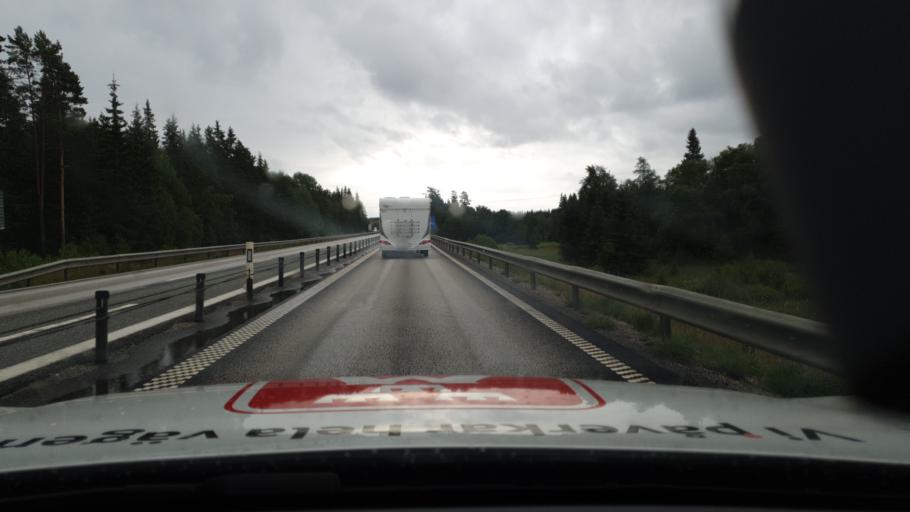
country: SE
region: Joenkoeping
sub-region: Nassjo Kommun
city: Malmback
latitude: 57.6954
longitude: 14.4448
